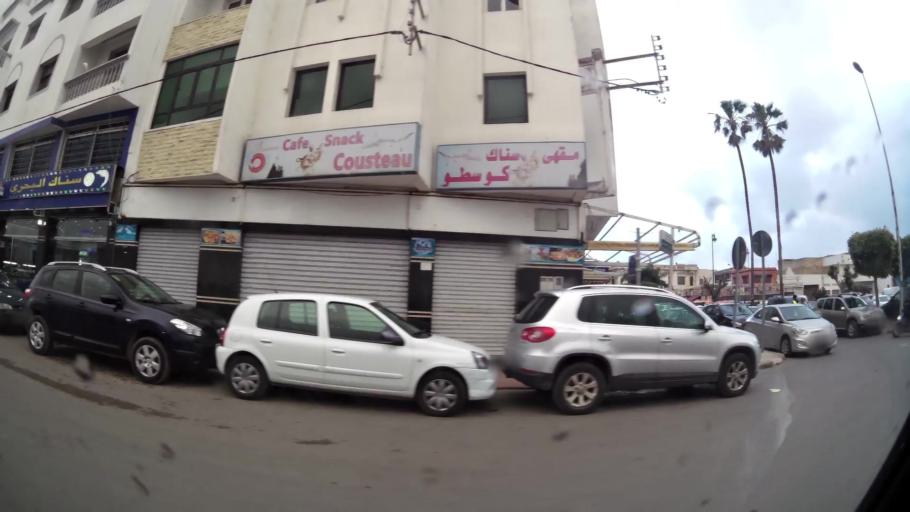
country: MA
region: Doukkala-Abda
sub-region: El-Jadida
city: El Jadida
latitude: 33.2548
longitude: -8.5032
